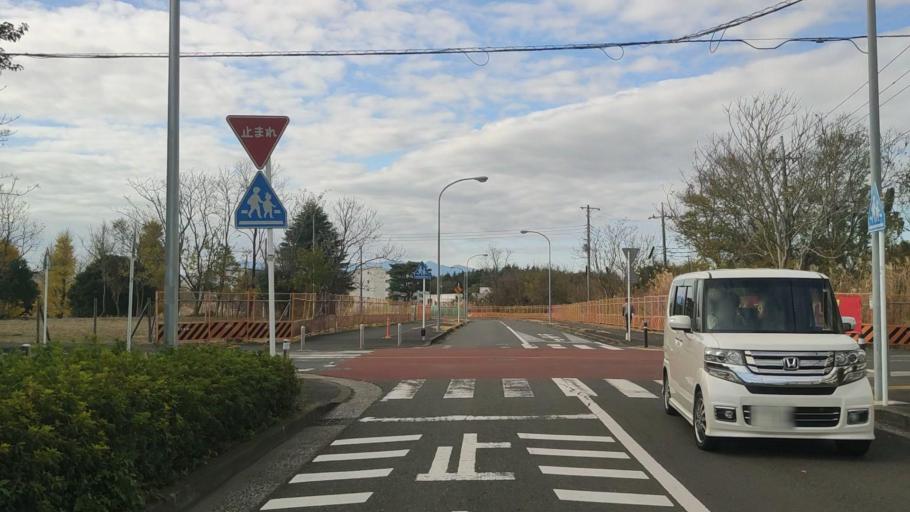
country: JP
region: Kanagawa
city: Minami-rinkan
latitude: 35.4831
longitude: 139.4892
